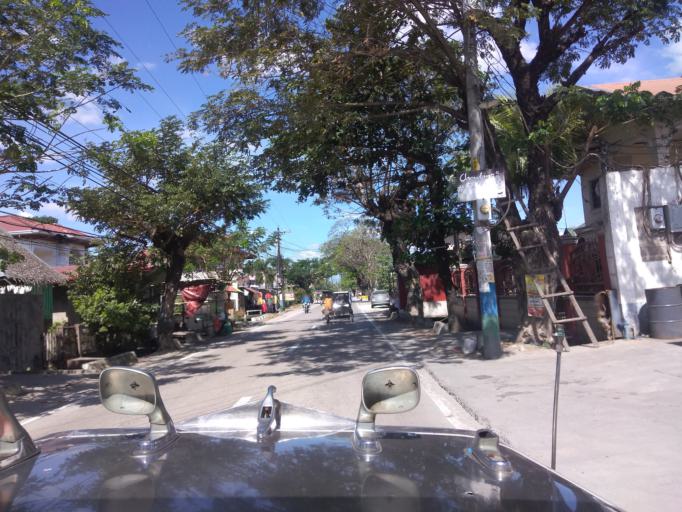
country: PH
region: Central Luzon
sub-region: Province of Pampanga
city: Santa Rita
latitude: 15.0005
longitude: 120.6108
